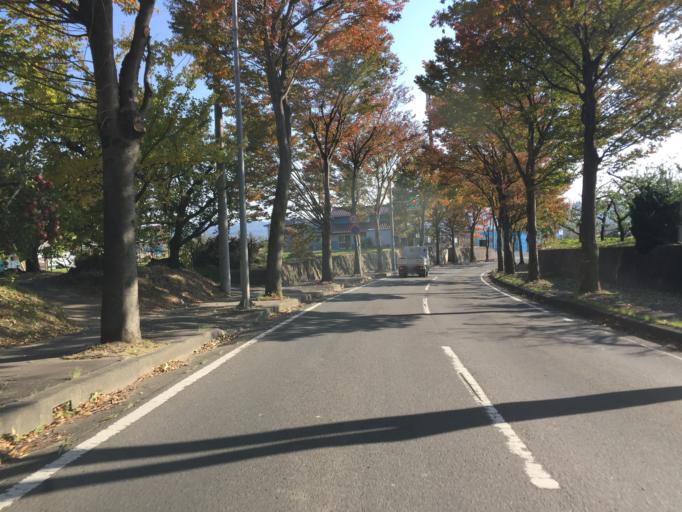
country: JP
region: Fukushima
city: Fukushima-shi
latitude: 37.8306
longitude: 140.4658
